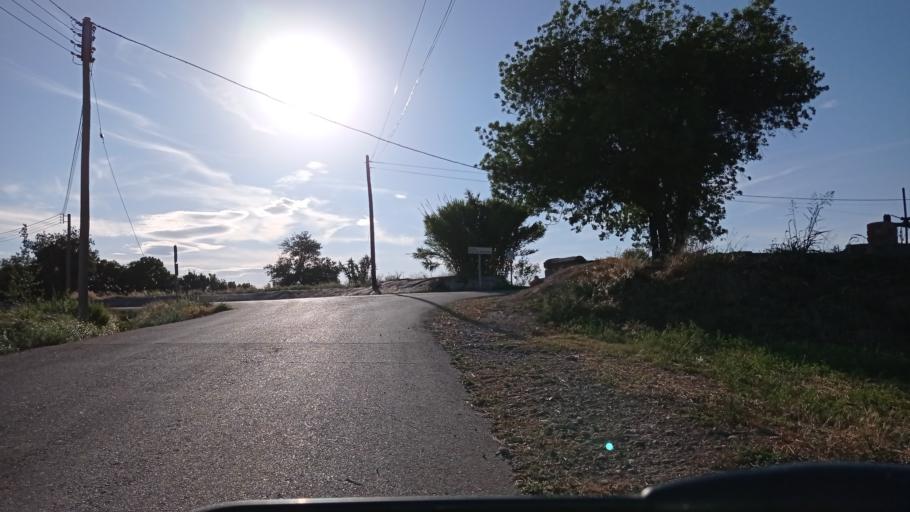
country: ES
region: Aragon
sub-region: Provincia de Zaragoza
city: Oliver-Valdefierro, Oliver, Valdefierro
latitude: 41.6667
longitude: -0.9640
